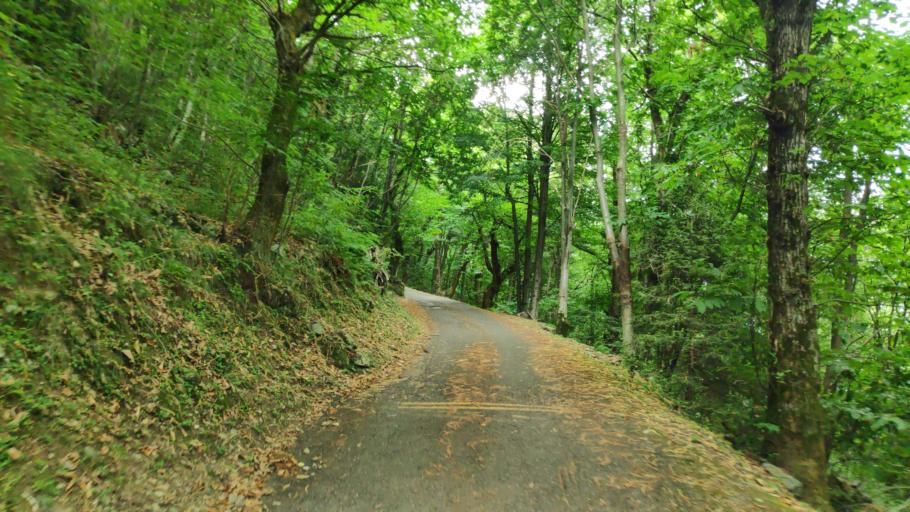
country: IT
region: Lombardy
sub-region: Provincia di Sondrio
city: Prata Camportaccio
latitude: 46.3010
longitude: 9.4017
